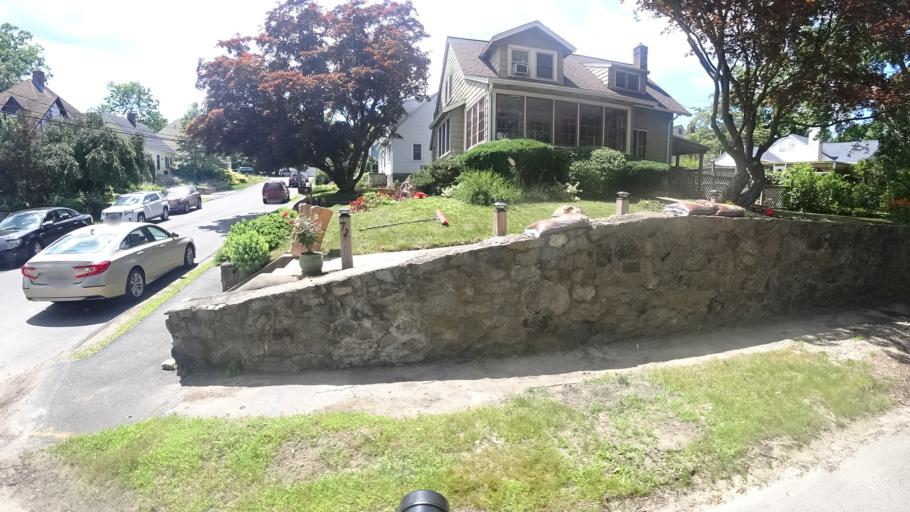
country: US
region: Massachusetts
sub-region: Norfolk County
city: Dedham
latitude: 42.2723
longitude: -71.1756
